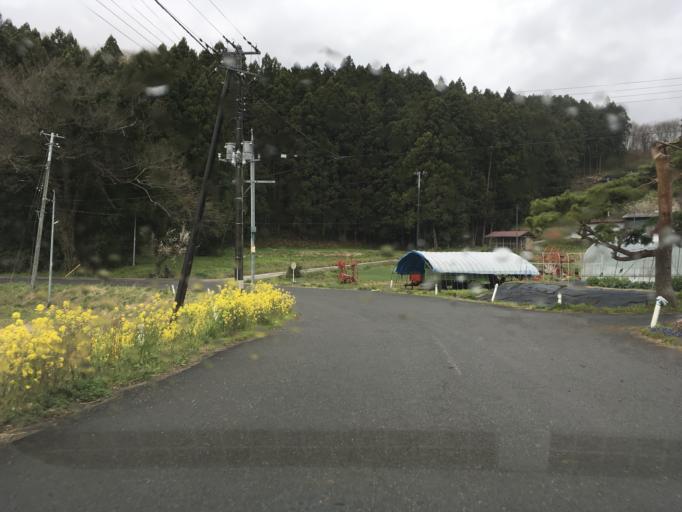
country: JP
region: Iwate
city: Ichinoseki
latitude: 38.7519
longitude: 141.2249
